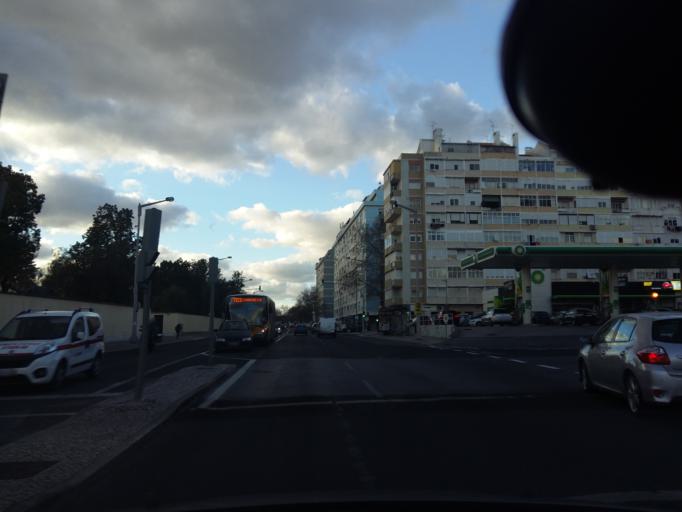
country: PT
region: Lisbon
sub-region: Odivelas
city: Pontinha
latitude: 38.7586
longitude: -9.1803
